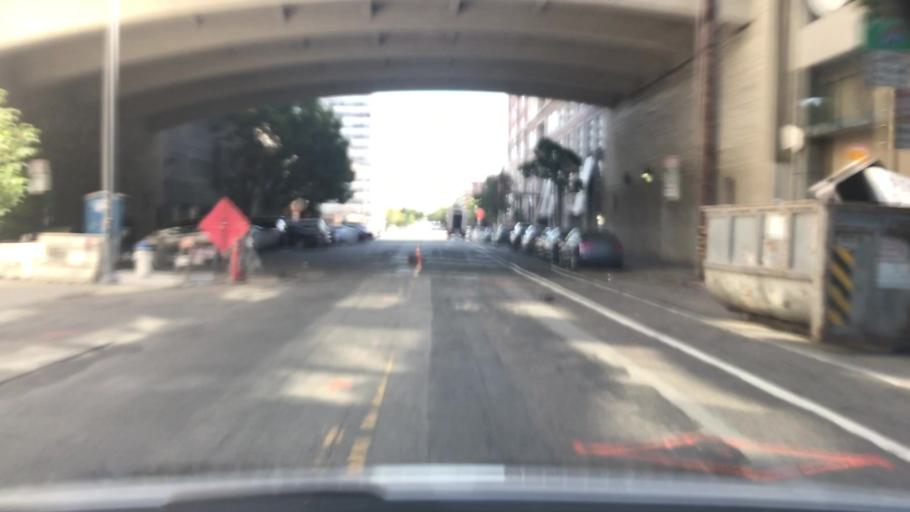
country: US
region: California
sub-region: San Francisco County
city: San Francisco
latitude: 37.7878
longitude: -122.3916
